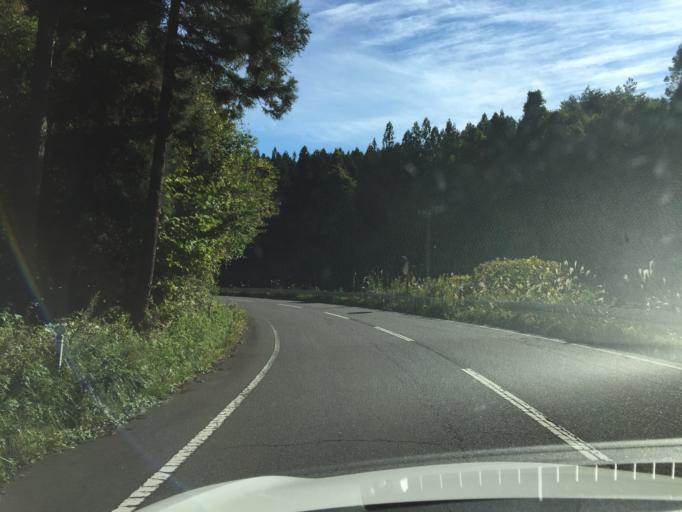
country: JP
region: Fukushima
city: Ishikawa
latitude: 37.1643
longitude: 140.5923
